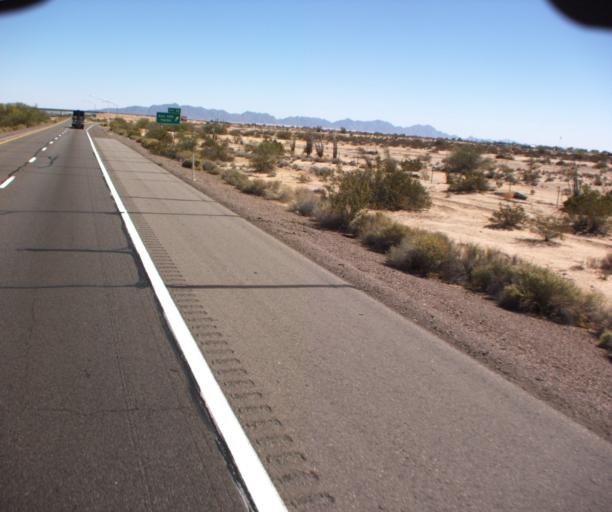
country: US
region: Arizona
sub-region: Yuma County
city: Wellton
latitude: 32.6923
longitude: -113.9604
